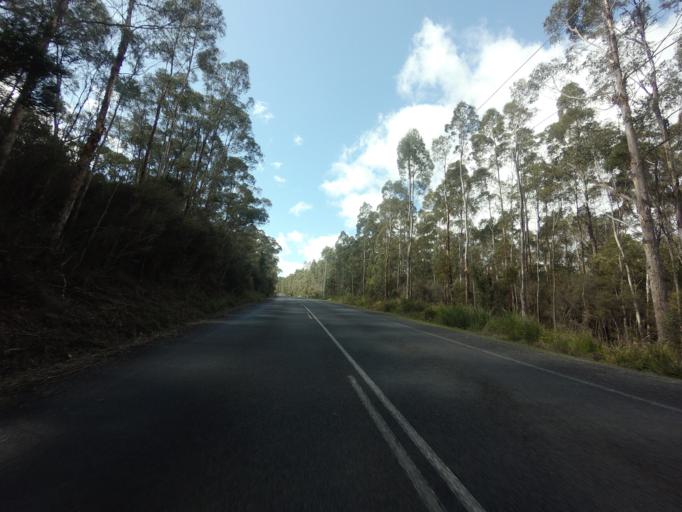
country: AU
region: Tasmania
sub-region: Huon Valley
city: Geeveston
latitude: -43.4151
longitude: 146.9366
